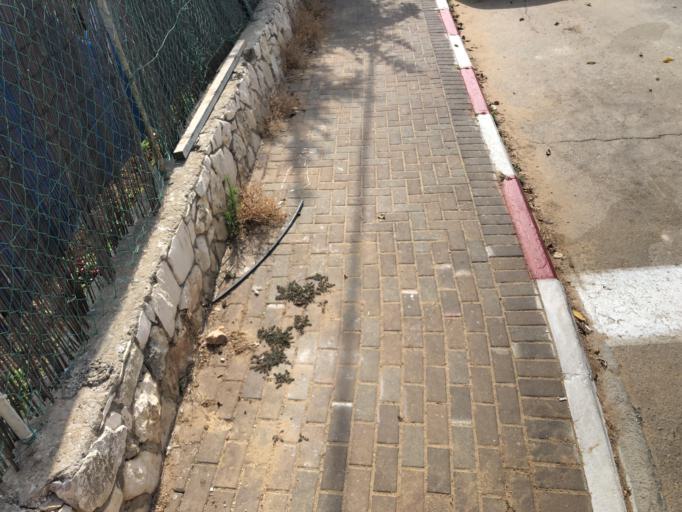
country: IL
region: Central District
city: Yehud
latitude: 32.0332
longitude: 34.8945
